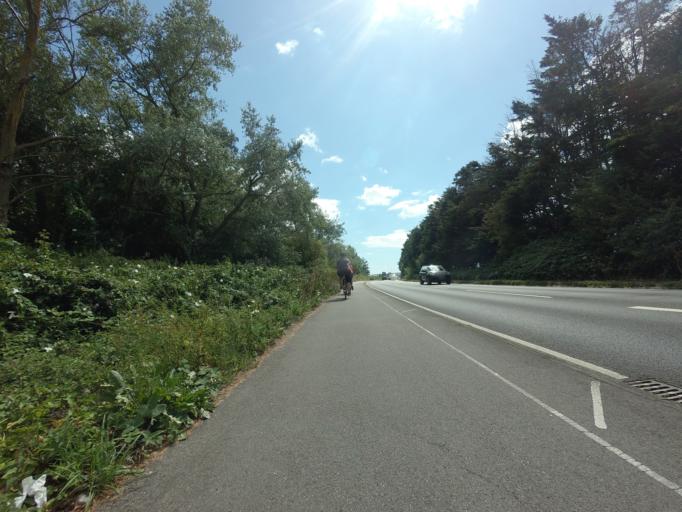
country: GB
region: England
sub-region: East Sussex
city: Pevensey
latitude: 50.8033
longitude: 0.3346
